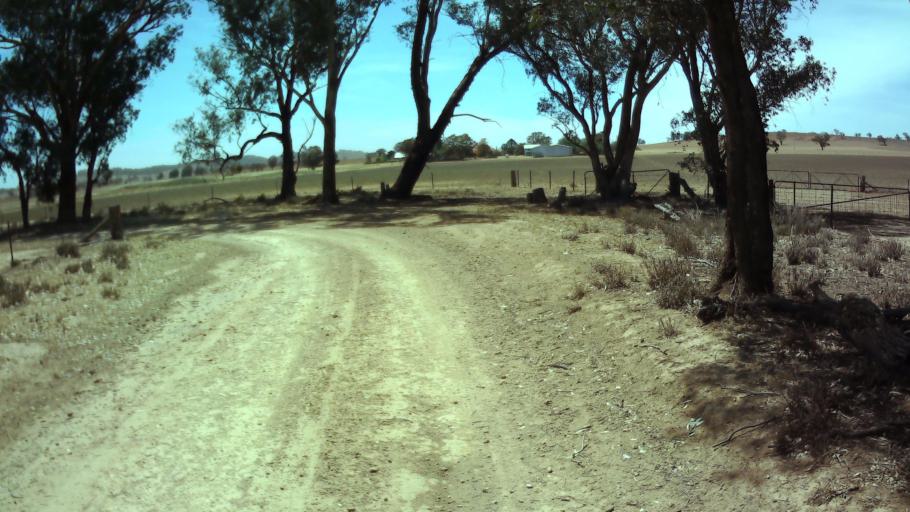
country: AU
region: New South Wales
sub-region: Weddin
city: Grenfell
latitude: -33.9927
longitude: 148.1632
